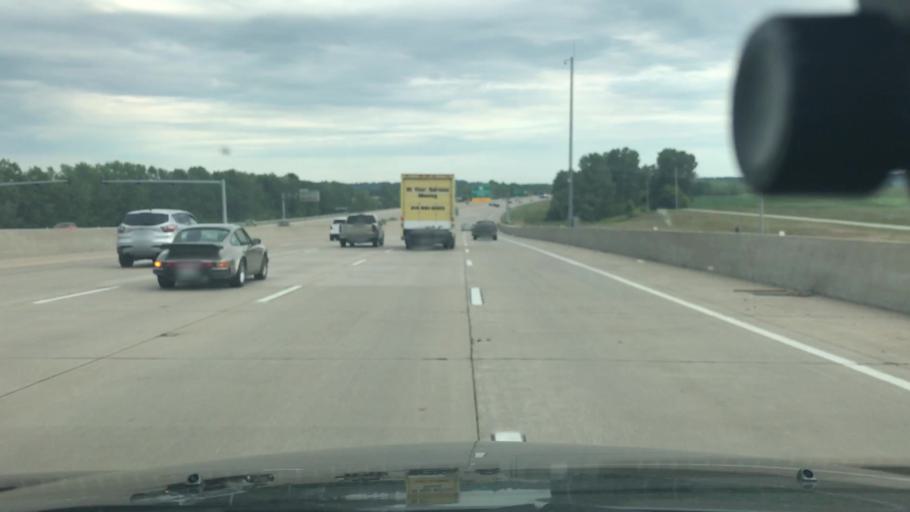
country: US
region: Missouri
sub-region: Saint Charles County
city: Saint Charles
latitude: 38.7300
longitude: -90.5173
